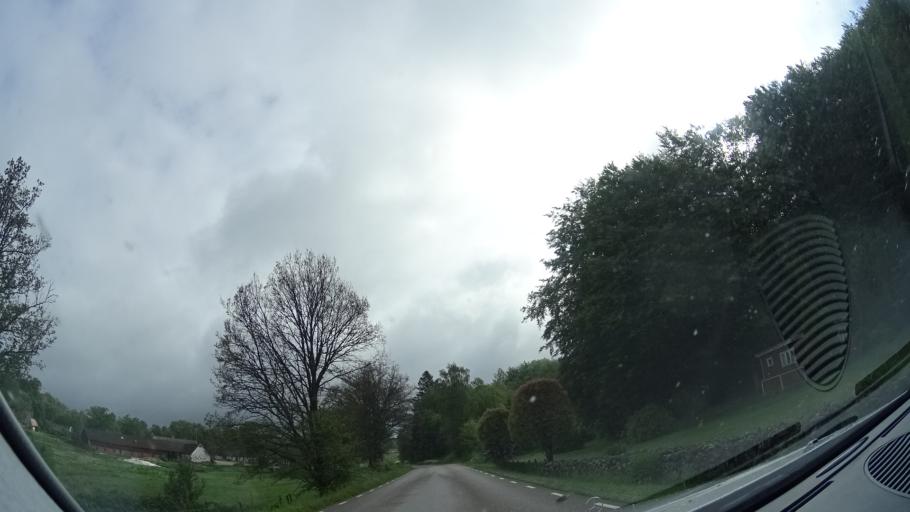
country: SE
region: Skane
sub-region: Hoors Kommun
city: Hoeoer
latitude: 55.9616
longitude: 13.4582
